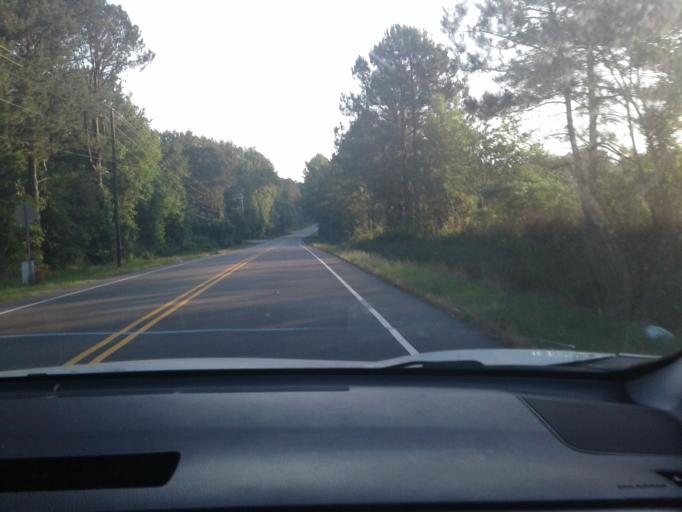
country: US
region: North Carolina
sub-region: Wake County
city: Fuquay-Varina
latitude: 35.5442
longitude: -78.8165
